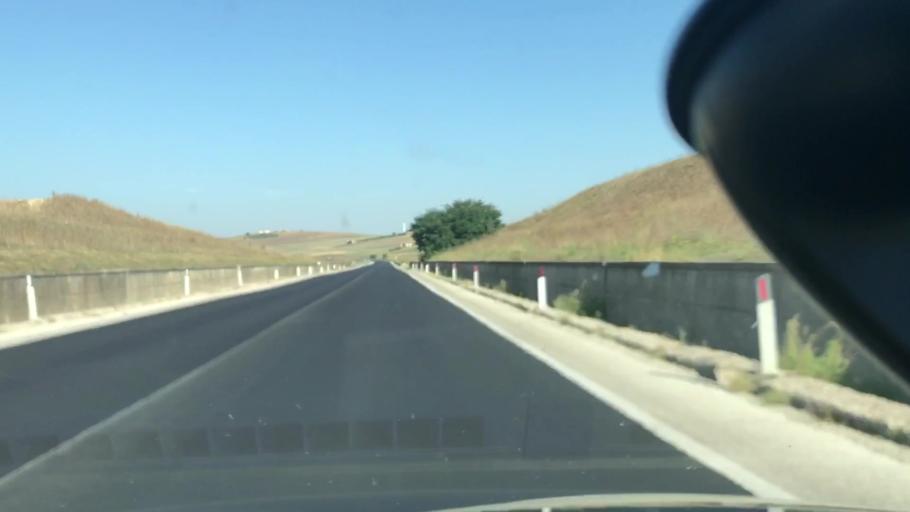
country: IT
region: Apulia
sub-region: Provincia di Barletta - Andria - Trani
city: Spinazzola
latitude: 40.9143
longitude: 16.1039
